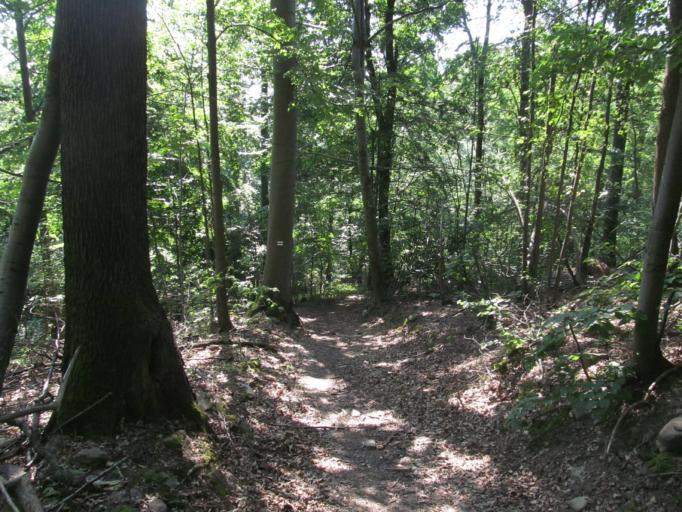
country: HU
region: Pest
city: Pilisszentkereszt
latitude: 47.7057
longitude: 18.9287
